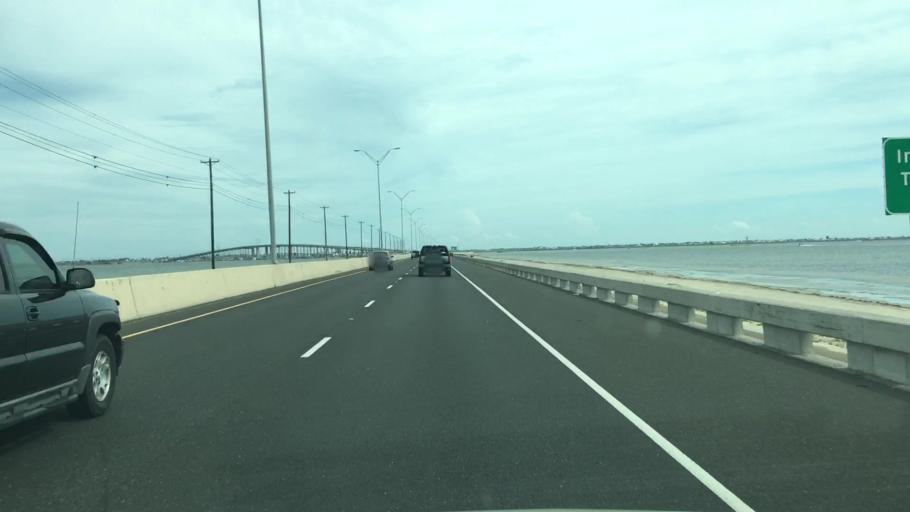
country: US
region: Texas
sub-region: Nueces County
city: Corpus Christi
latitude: 27.6459
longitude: -97.2508
